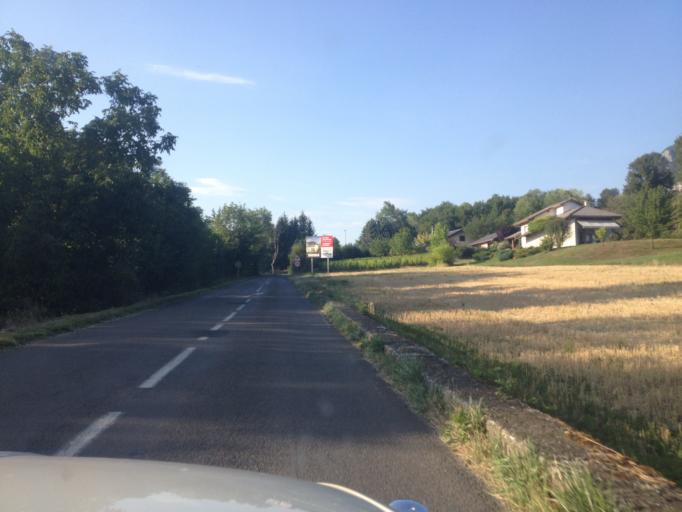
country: FR
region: Rhone-Alpes
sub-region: Departement de la Savoie
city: Mery
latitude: 45.6537
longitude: 5.9381
